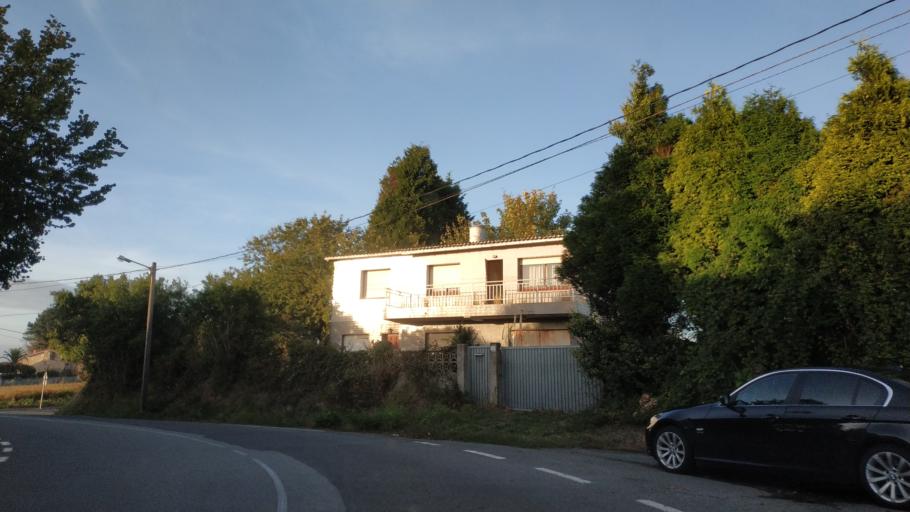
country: ES
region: Galicia
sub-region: Provincia da Coruna
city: Oleiros
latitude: 43.3611
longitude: -8.3417
